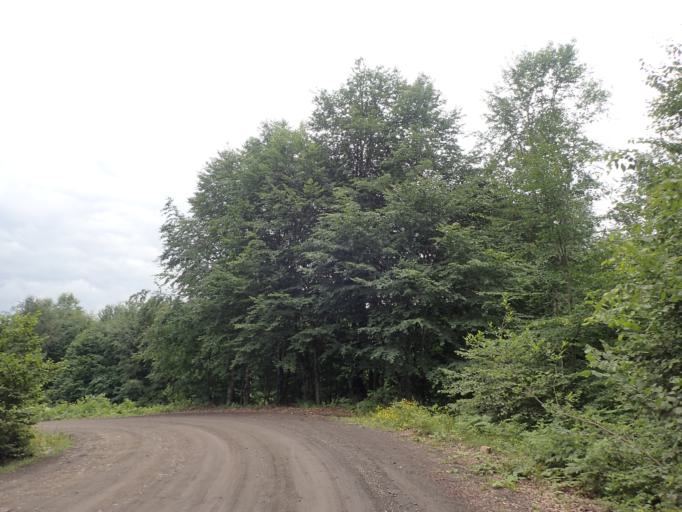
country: TR
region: Ordu
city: Akkus
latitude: 40.8033
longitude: 37.0765
